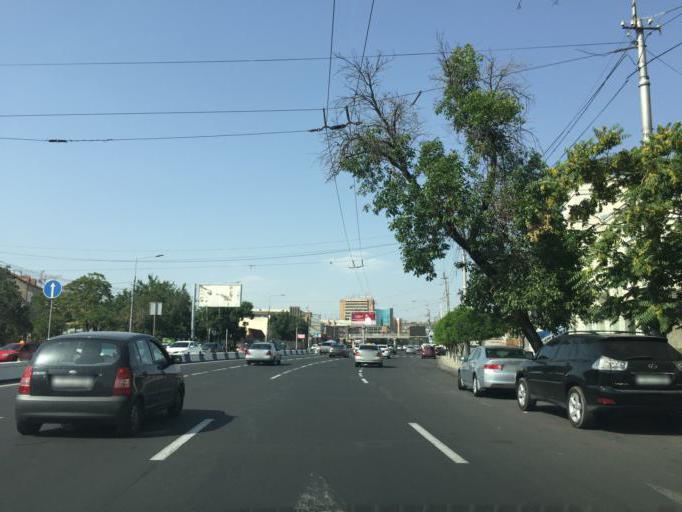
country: AM
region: Yerevan
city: Yerevan
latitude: 40.1647
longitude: 44.5047
